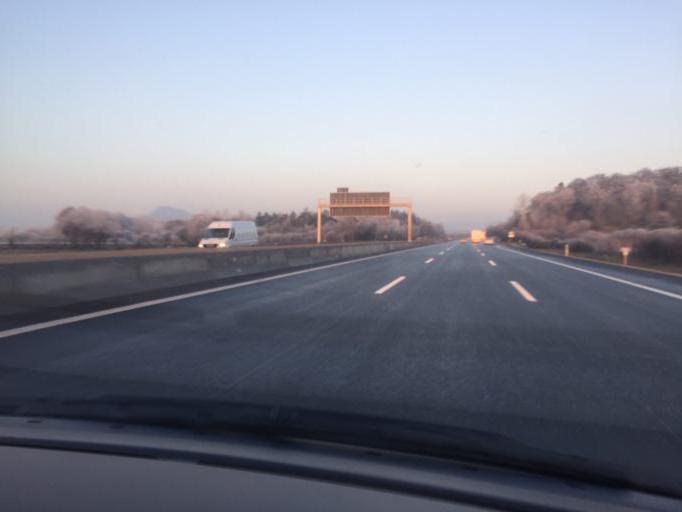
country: DE
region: Baden-Wuerttemberg
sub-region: Freiburg Region
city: Aach
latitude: 47.8219
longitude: 8.8387
